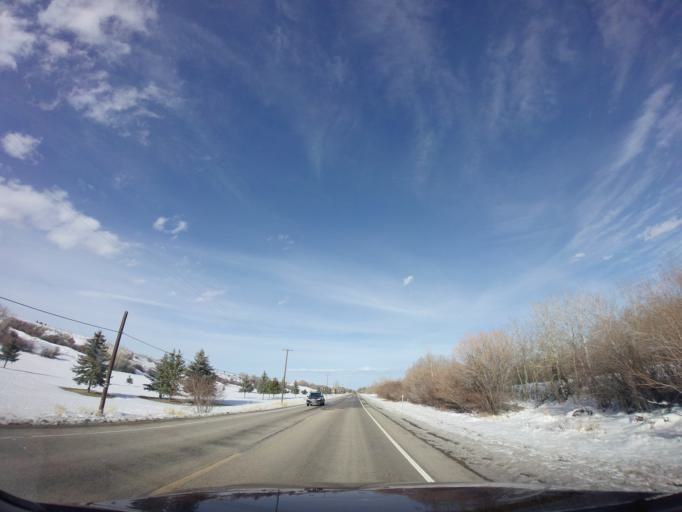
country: US
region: Montana
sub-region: Carbon County
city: Red Lodge
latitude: 45.2049
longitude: -109.2446
